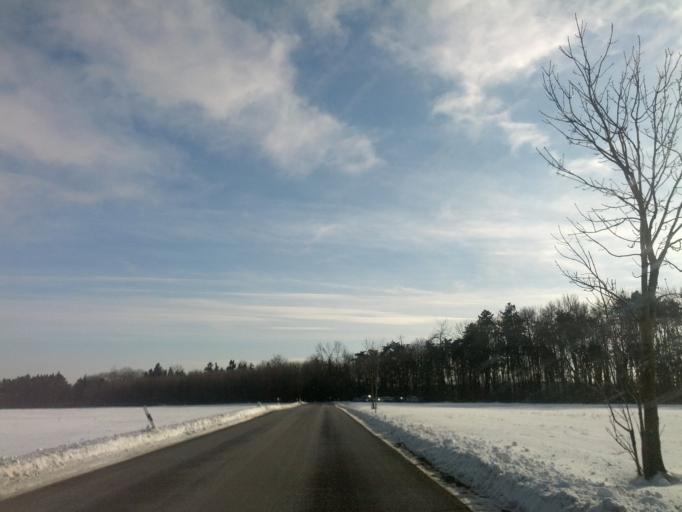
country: DE
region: Thuringia
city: Weberstedt
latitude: 51.0552
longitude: 10.4945
